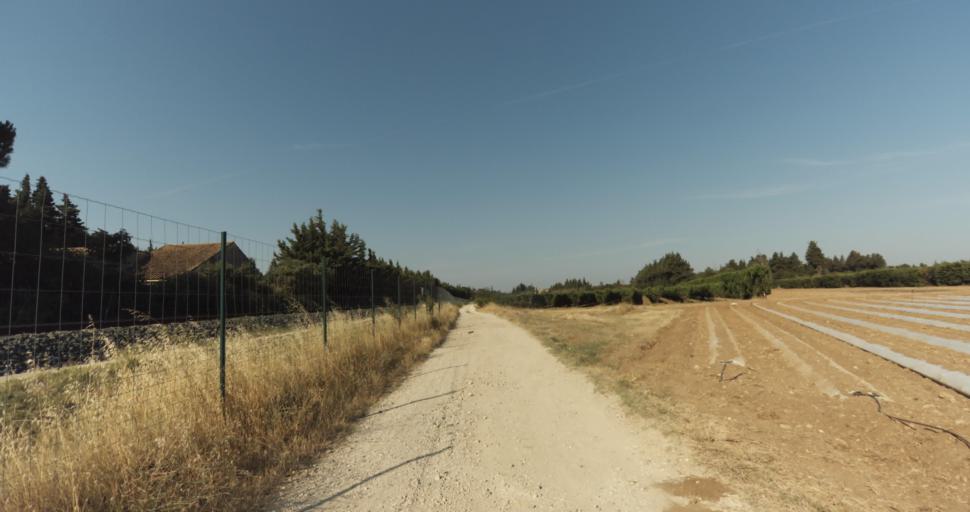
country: FR
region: Provence-Alpes-Cote d'Azur
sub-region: Departement du Vaucluse
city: Monteux
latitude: 44.0343
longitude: 5.0235
